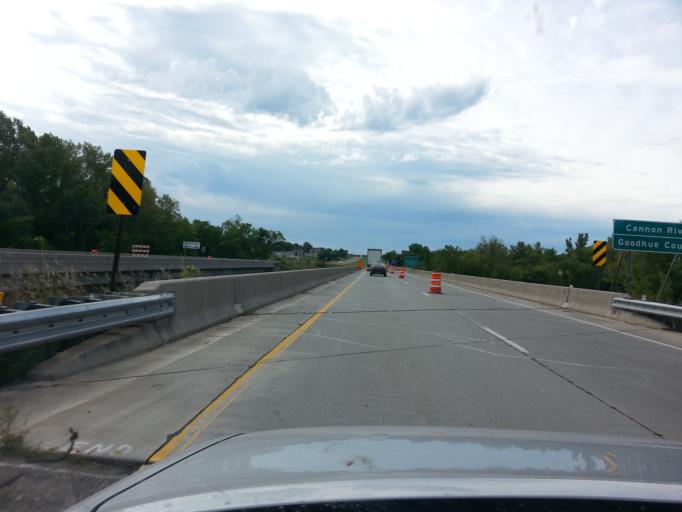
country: US
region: Minnesota
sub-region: Goodhue County
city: Cannon Falls
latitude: 44.5181
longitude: -92.9233
